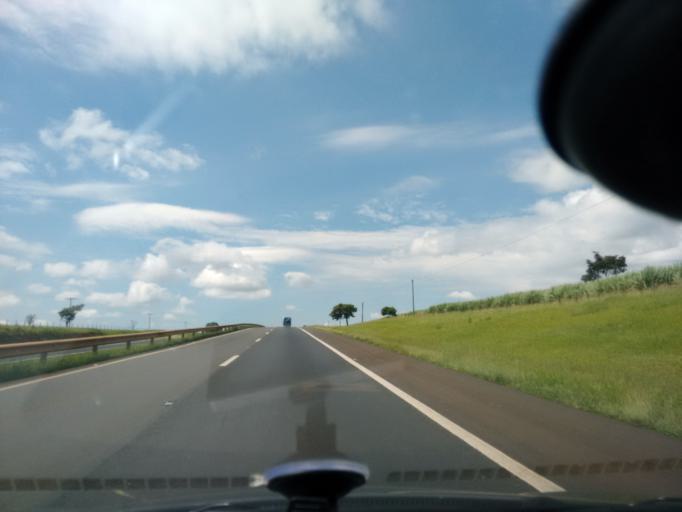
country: BR
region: Sao Paulo
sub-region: Ibate
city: Ibate
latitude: -21.9198
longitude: -48.0357
